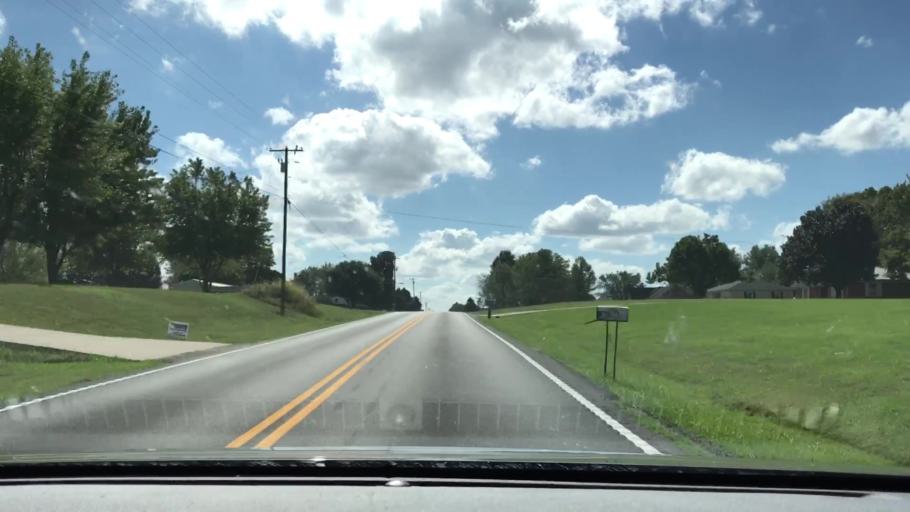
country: US
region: Kentucky
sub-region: Graves County
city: Mayfield
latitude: 36.8046
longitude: -88.5954
